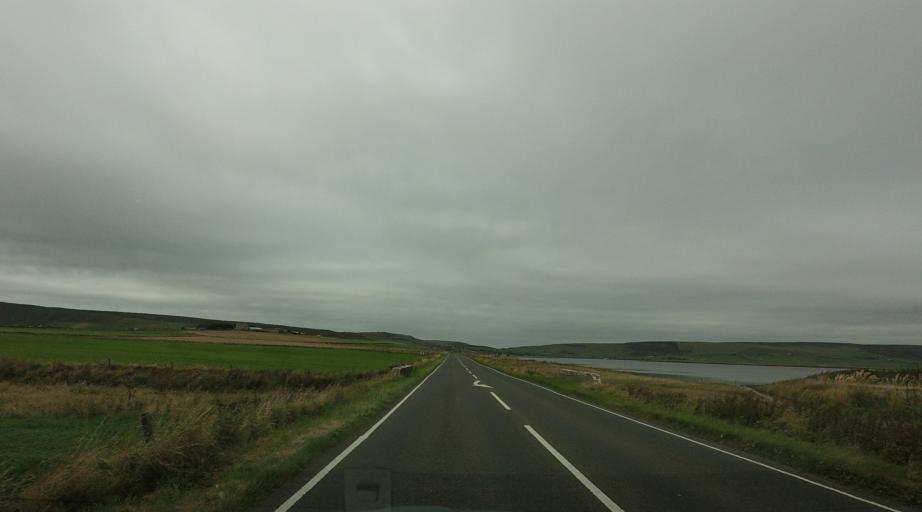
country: GB
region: Scotland
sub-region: Orkney Islands
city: Orkney
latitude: 58.9952
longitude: -3.0667
